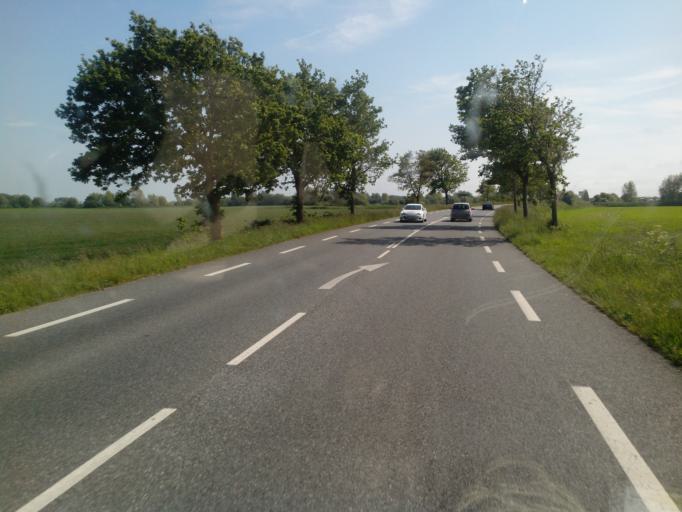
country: FR
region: Picardie
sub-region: Departement de la Somme
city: Quend
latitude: 50.3472
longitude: 1.6469
